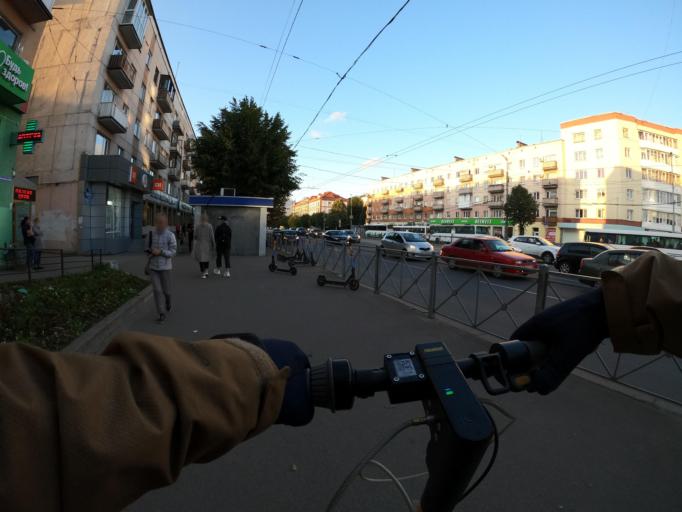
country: RU
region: Kaliningrad
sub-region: Gorod Kaliningrad
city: Kaliningrad
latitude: 54.6993
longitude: 20.5027
